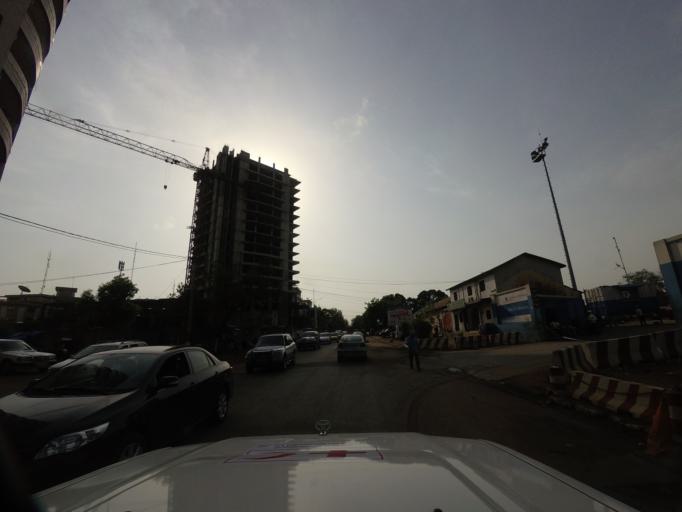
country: GN
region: Conakry
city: Camayenne
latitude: 9.5143
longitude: -13.7100
